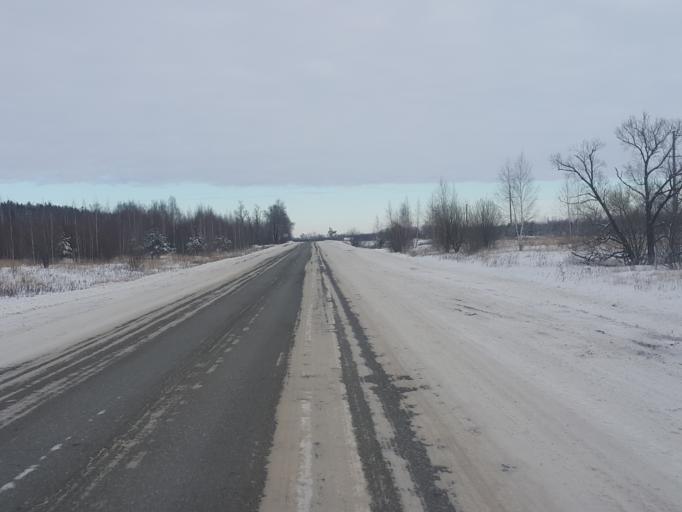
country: RU
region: Tambov
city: Platonovka
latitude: 52.8671
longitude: 41.8568
